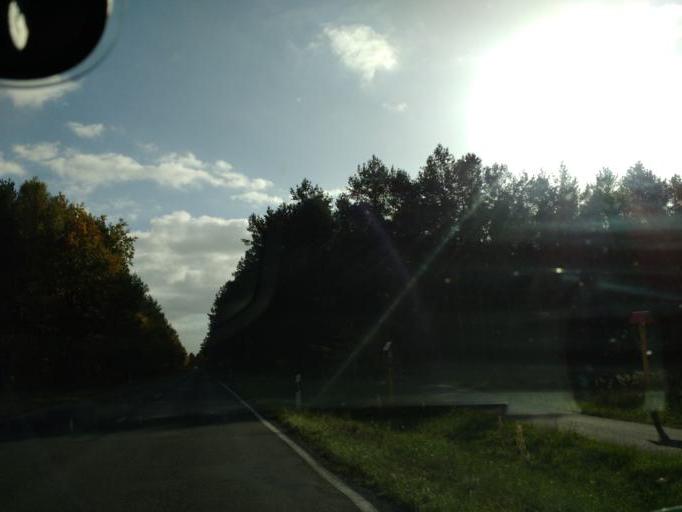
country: DE
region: Brandenburg
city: Spreenhagen
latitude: 52.3704
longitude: 13.8368
